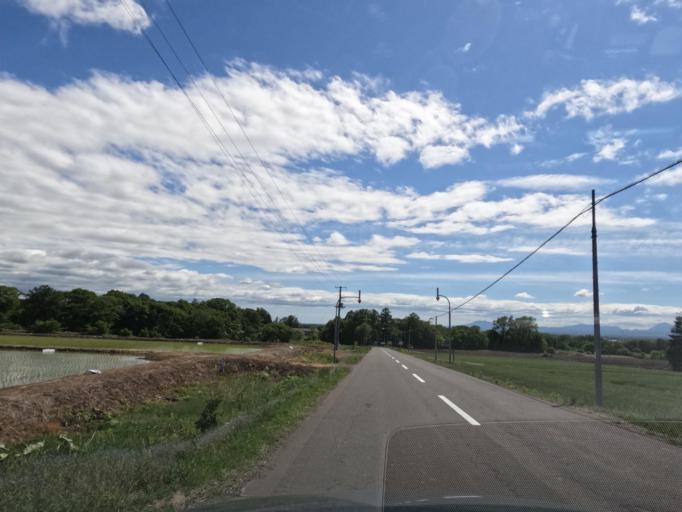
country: JP
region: Hokkaido
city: Kitahiroshima
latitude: 42.9952
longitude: 141.7285
